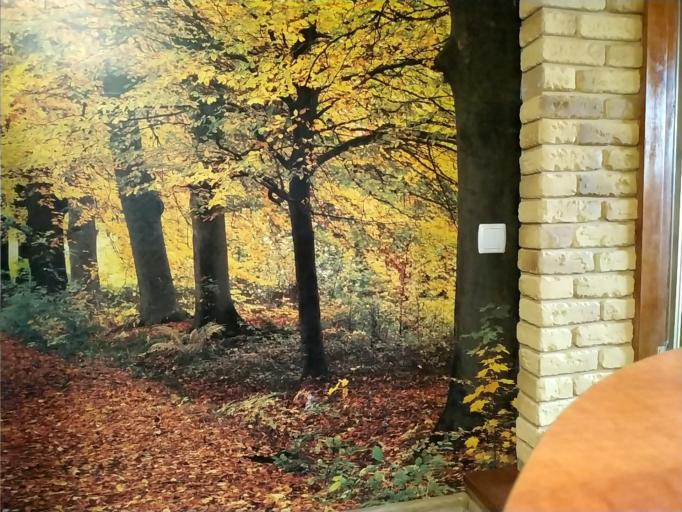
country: RU
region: Leningrad
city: Tolmachevo
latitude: 58.9347
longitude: 29.6997
